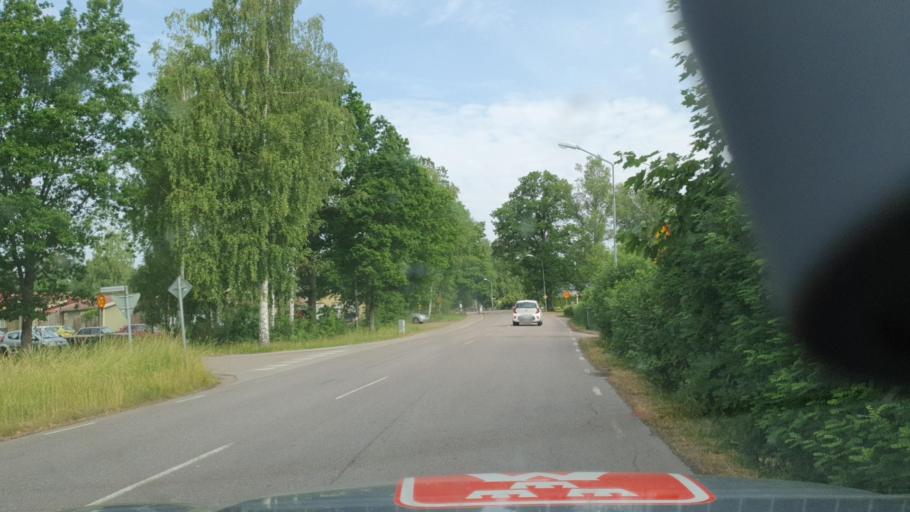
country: SE
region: Kalmar
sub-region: Kalmar Kommun
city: Trekanten
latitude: 56.6222
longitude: 16.0443
